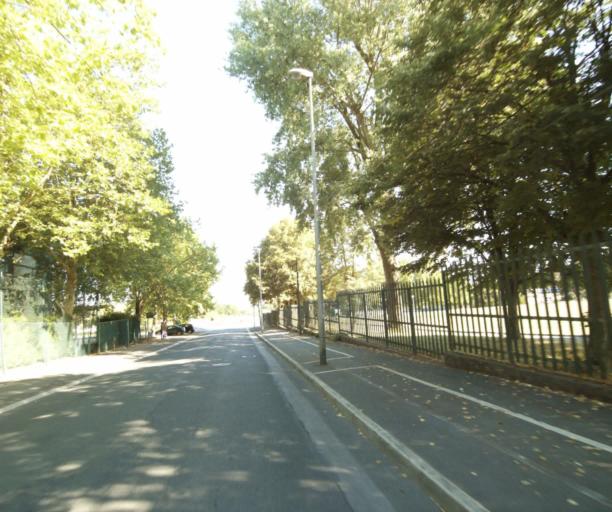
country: FR
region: Ile-de-France
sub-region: Departement de Seine-et-Marne
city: Lagny-sur-Marne
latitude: 48.8710
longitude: 2.7182
